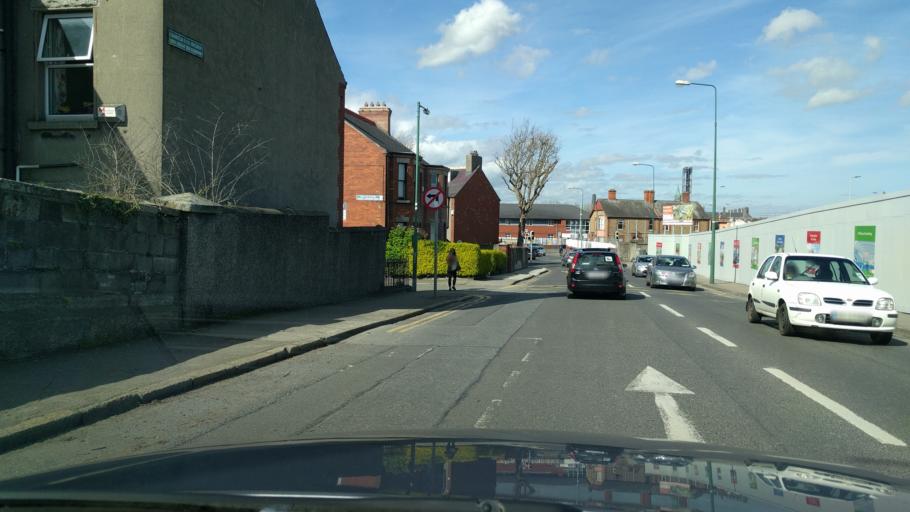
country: IE
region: Leinster
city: Rialto
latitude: 53.3379
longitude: -6.2994
